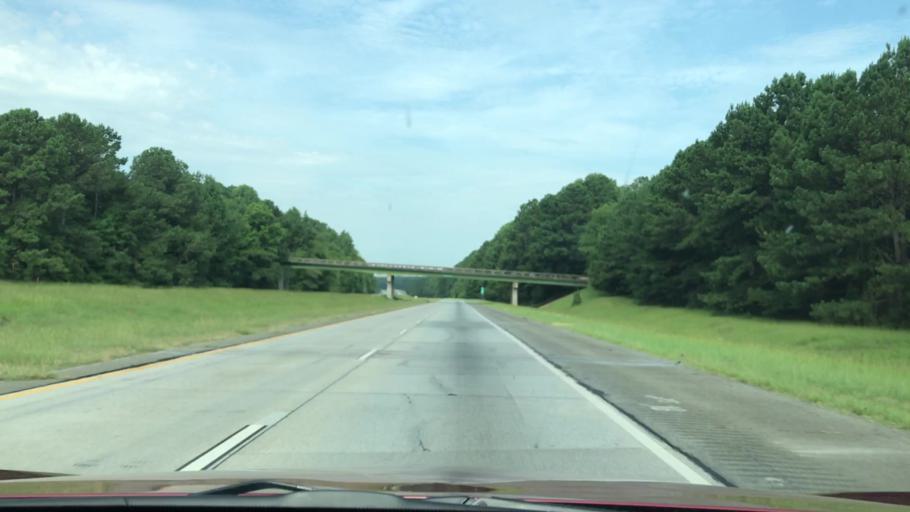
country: US
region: Georgia
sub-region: Warren County
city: Firing Range
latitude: 33.5043
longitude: -82.7471
